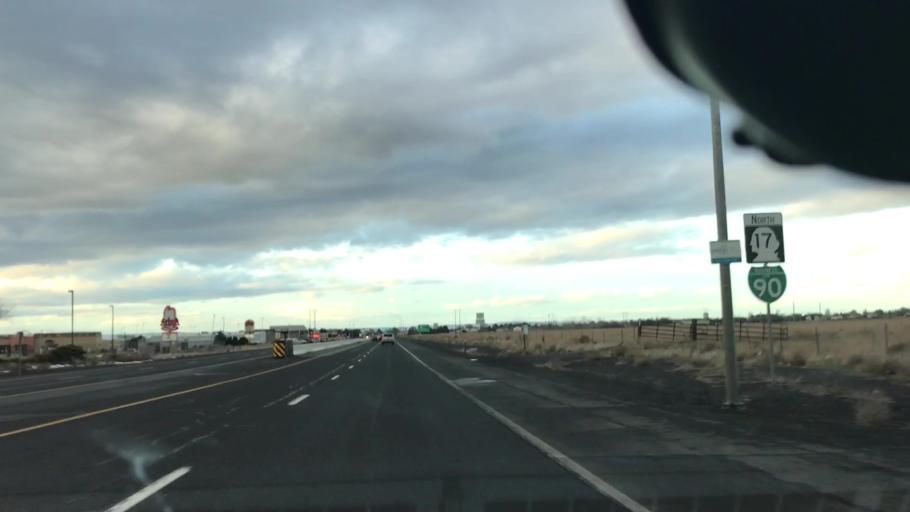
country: US
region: Washington
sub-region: Grant County
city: Moses Lake
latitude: 47.1024
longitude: -119.2473
